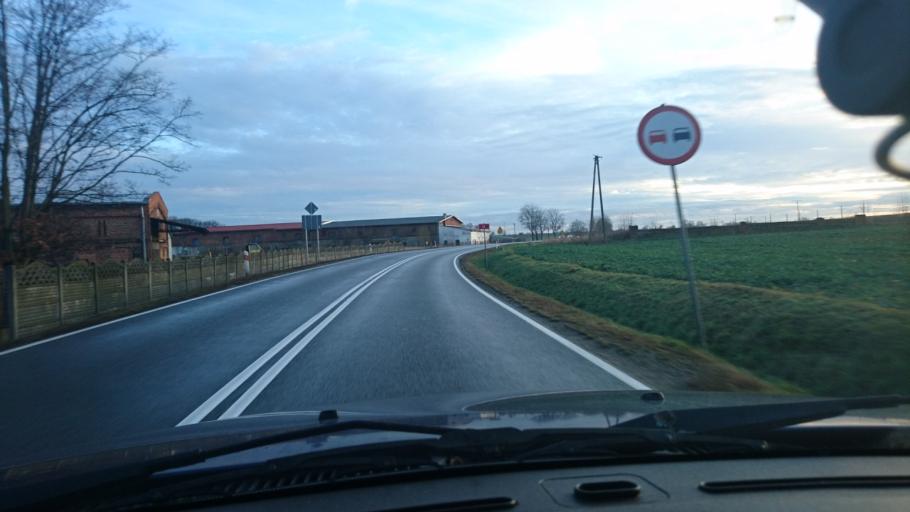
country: PL
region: Opole Voivodeship
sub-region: Powiat kluczborski
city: Byczyna
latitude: 51.1358
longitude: 18.1990
